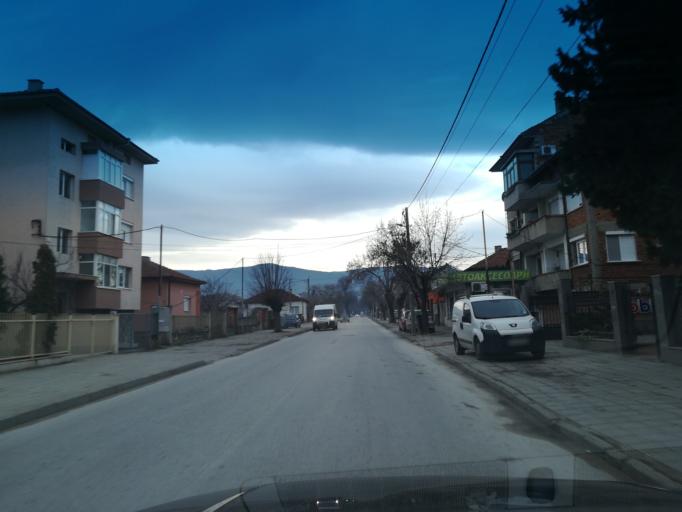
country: BG
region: Plovdiv
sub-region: Obshtina Plovdiv
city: Plovdiv
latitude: 42.1057
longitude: 24.7052
